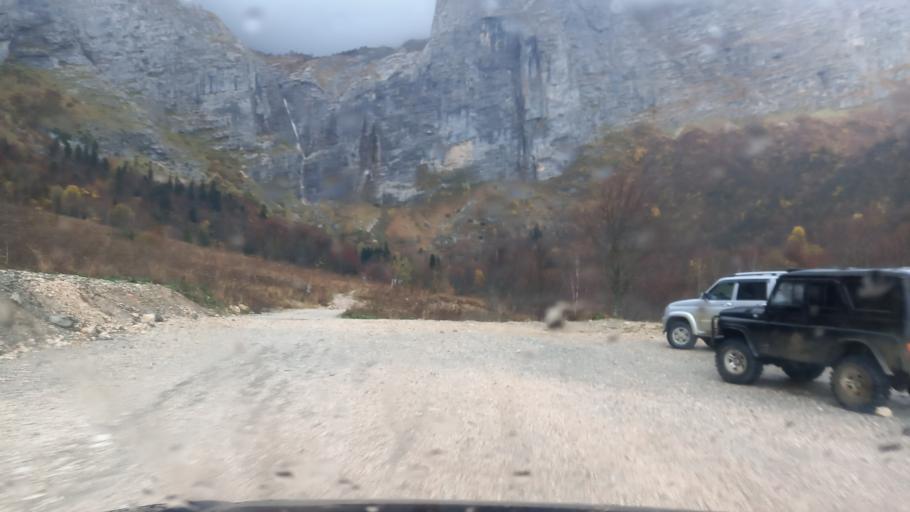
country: RU
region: Krasnodarskiy
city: Dagomys
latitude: 43.9792
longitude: 39.8716
